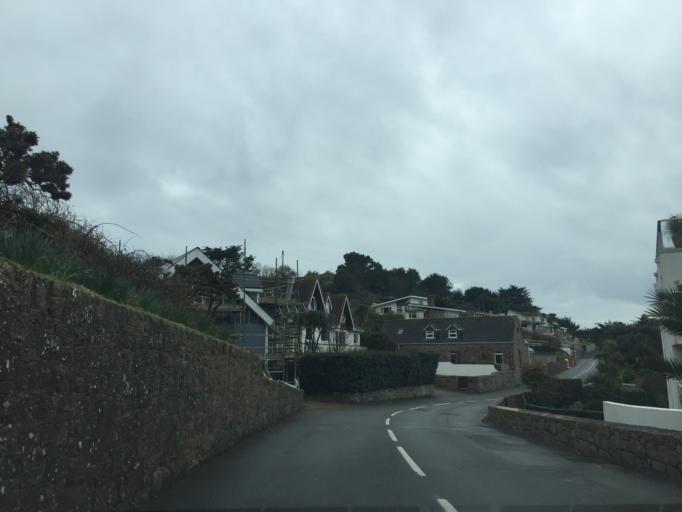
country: JE
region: St Helier
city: Saint Helier
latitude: 49.1841
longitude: -2.2329
